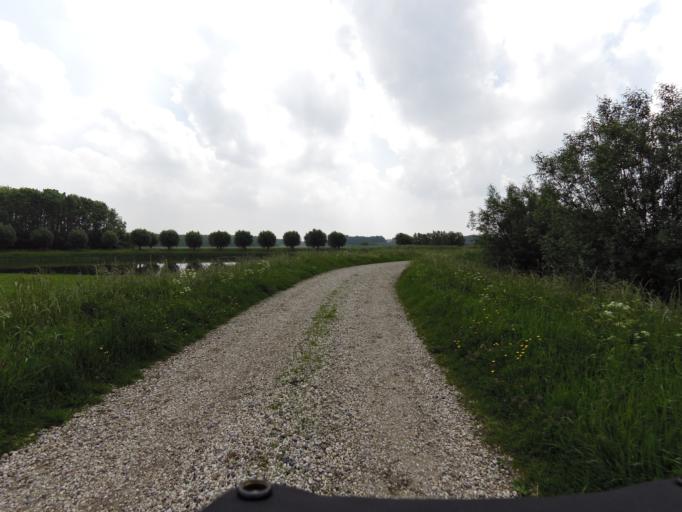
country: NL
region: South Holland
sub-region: Gemeente Spijkenisse
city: Spijkenisse
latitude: 51.8386
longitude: 4.2572
